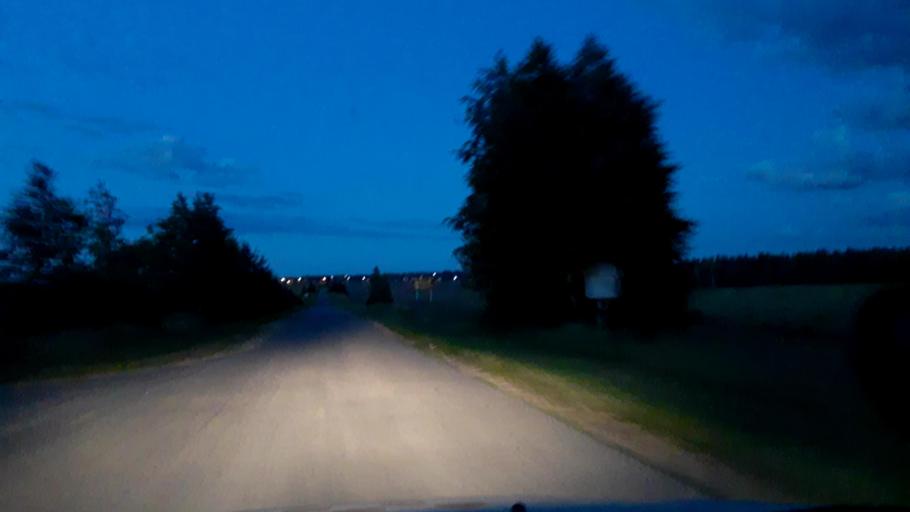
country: RU
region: Nizjnij Novgorod
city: Pamyat' Parizhskoy Kommuny
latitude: 56.0587
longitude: 44.4867
